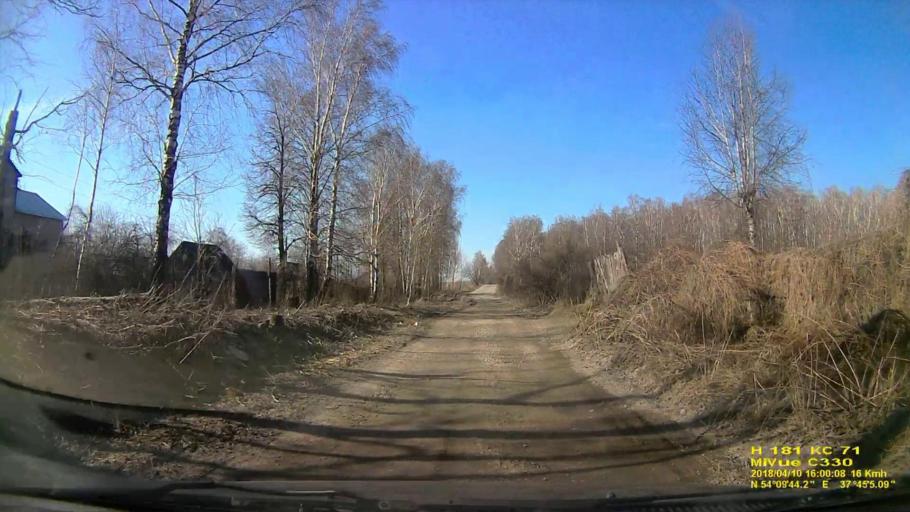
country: RU
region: Tula
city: Bolokhovo
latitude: 54.1623
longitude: 37.7514
